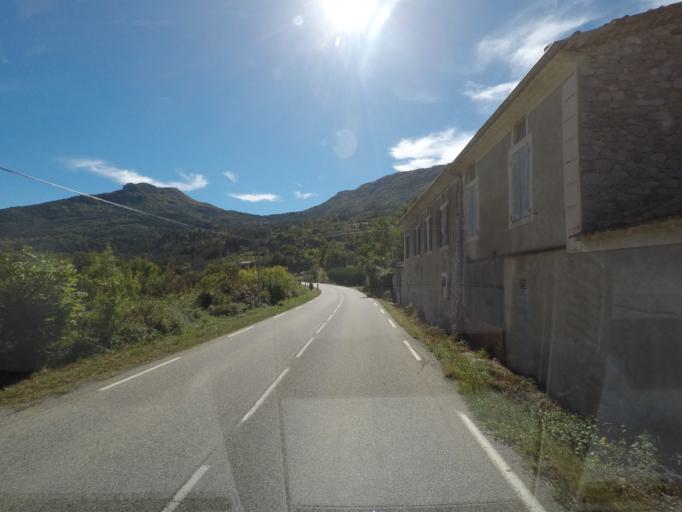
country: FR
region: Rhone-Alpes
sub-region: Departement de la Drome
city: Buis-les-Baronnies
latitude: 44.4003
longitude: 5.3501
